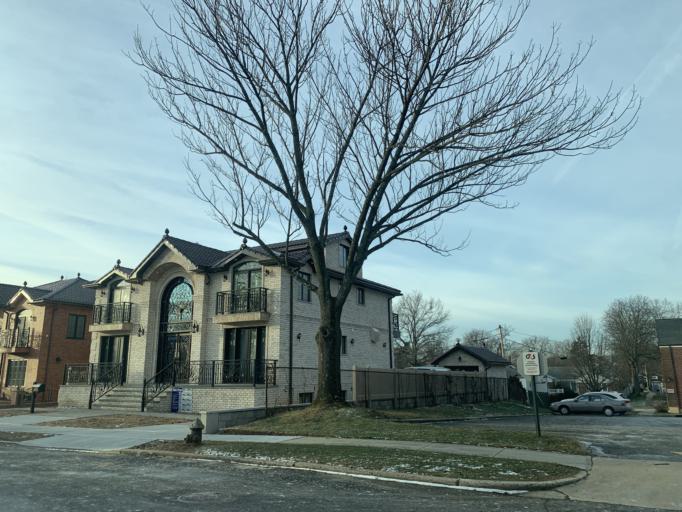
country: US
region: New York
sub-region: Nassau County
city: Lake Success
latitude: 40.7558
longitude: -73.7249
